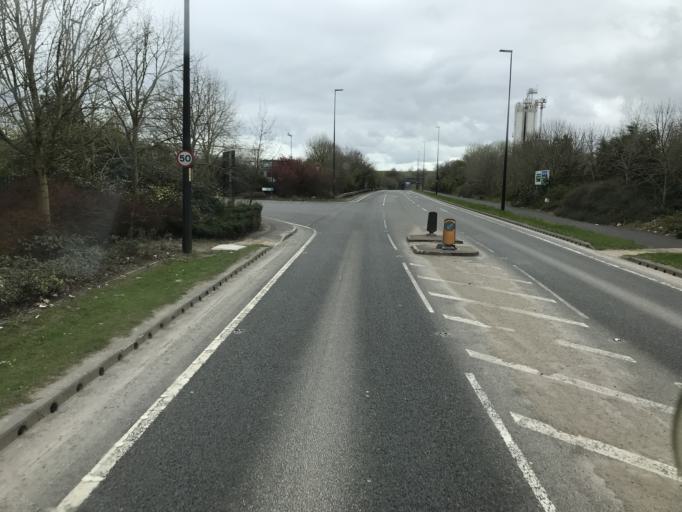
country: GB
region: England
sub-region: Trafford
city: Partington
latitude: 53.4283
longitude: -2.4261
